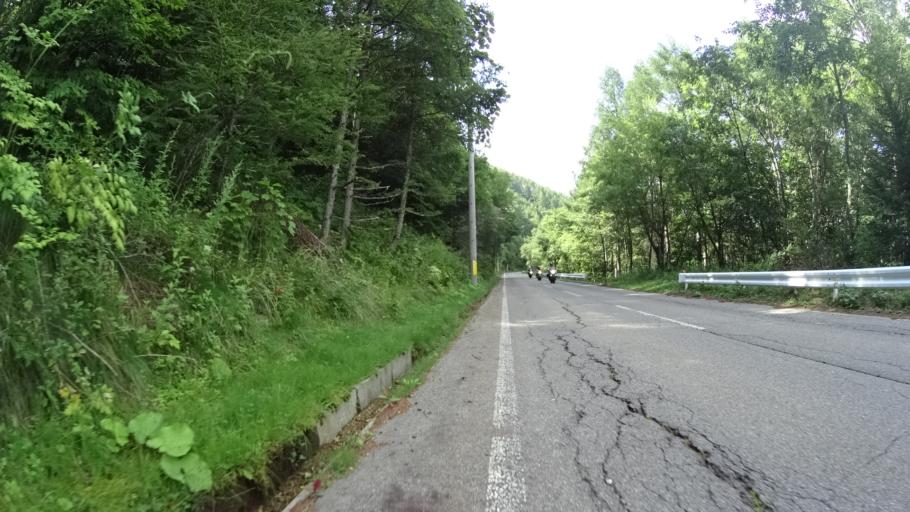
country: JP
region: Nagano
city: Saku
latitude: 36.0495
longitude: 138.4054
